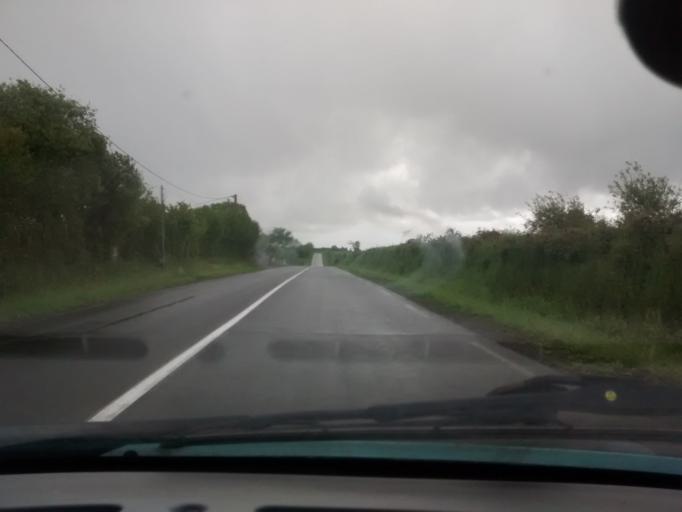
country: FR
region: Lower Normandy
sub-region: Departement de la Manche
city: Conde-sur-Vire
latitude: 49.0884
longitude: -1.0426
